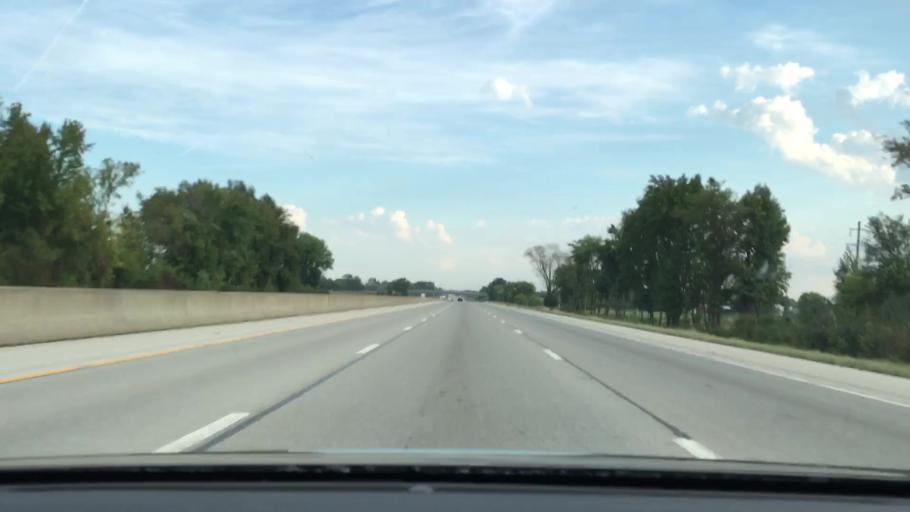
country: US
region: Kentucky
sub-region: Warren County
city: Plano
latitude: 36.8568
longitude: -86.4554
